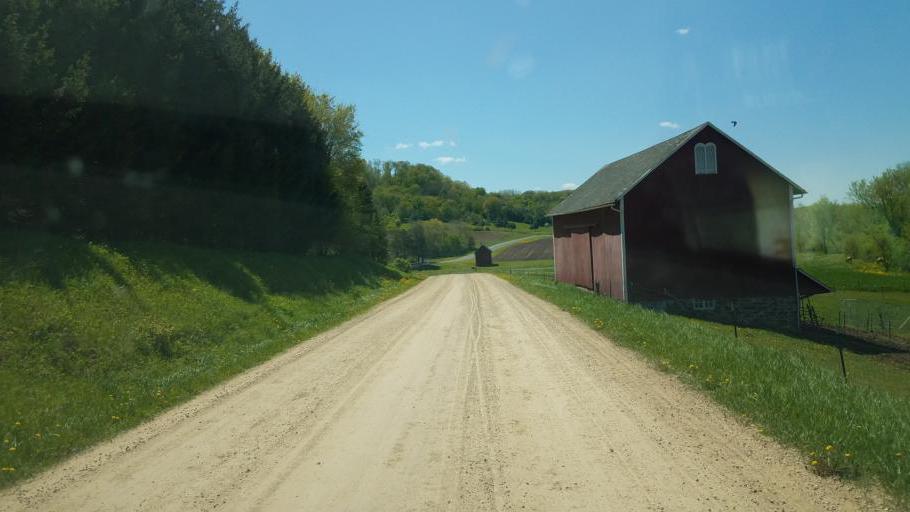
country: US
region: Wisconsin
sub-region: Vernon County
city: Hillsboro
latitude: 43.5657
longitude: -90.4177
